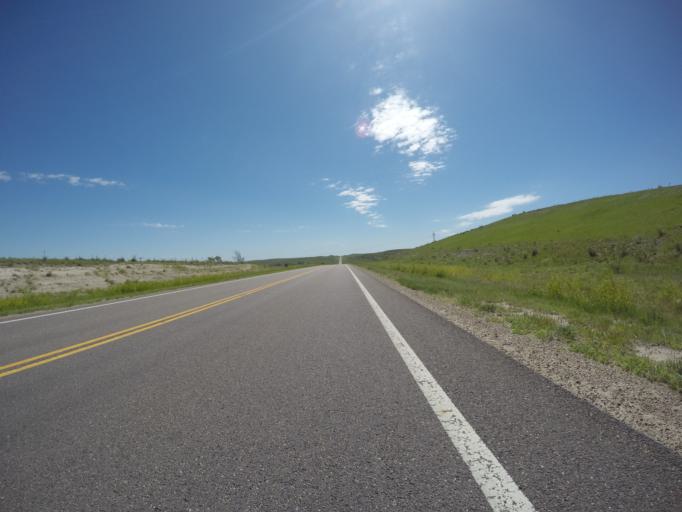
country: US
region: Kansas
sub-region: Rawlins County
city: Atwood
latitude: 39.8133
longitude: -101.0209
